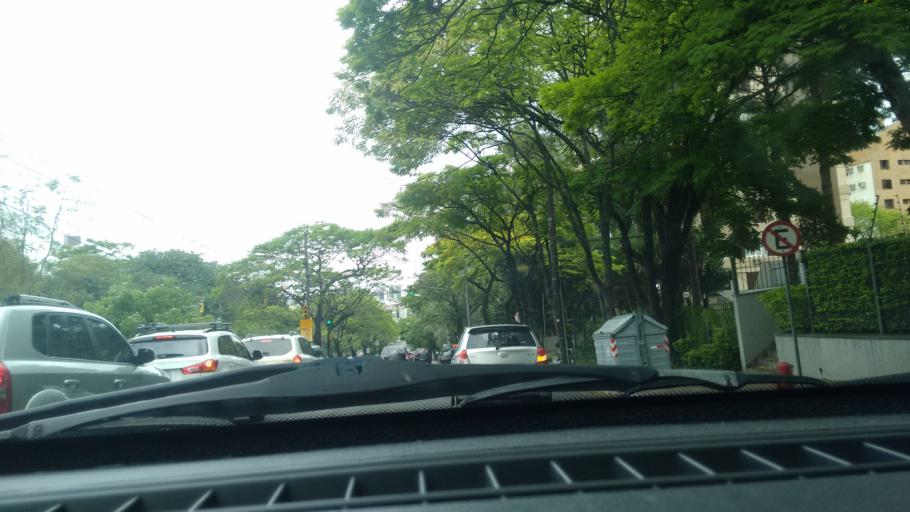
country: BR
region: Rio Grande do Sul
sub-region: Porto Alegre
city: Porto Alegre
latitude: -30.0313
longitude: -51.1837
